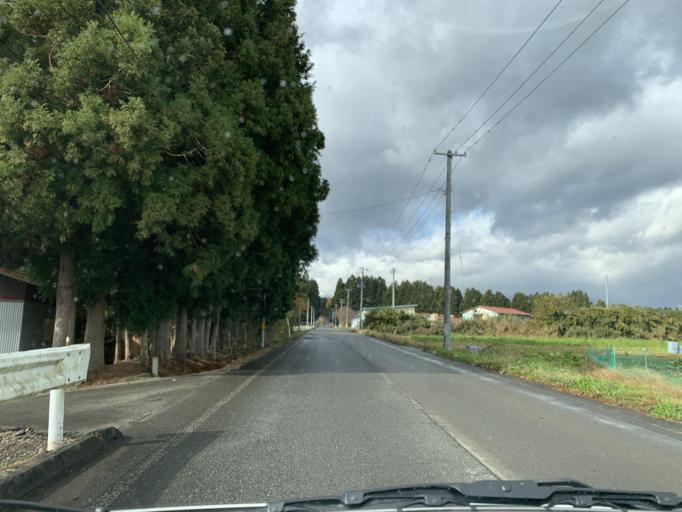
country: JP
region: Iwate
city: Mizusawa
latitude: 39.0989
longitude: 141.0015
